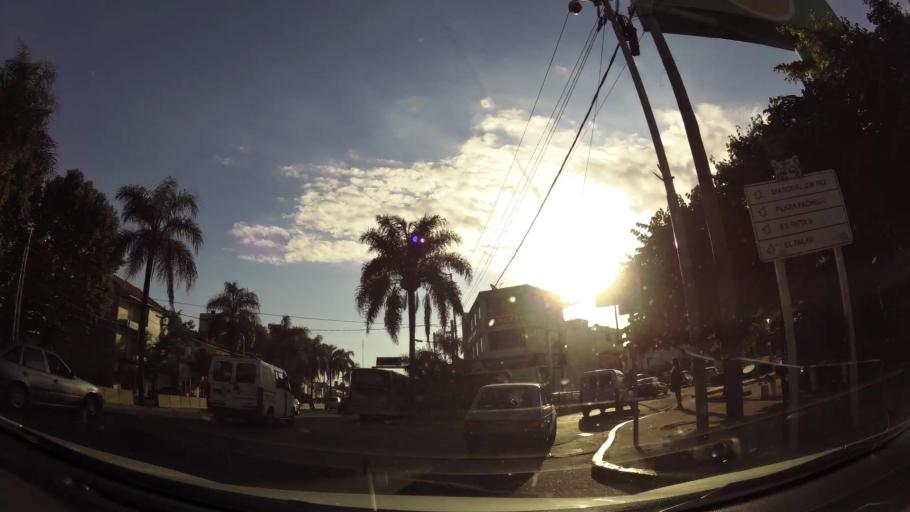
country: AR
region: Buenos Aires
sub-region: Partido de Tigre
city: Tigre
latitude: -34.4561
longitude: -58.6268
